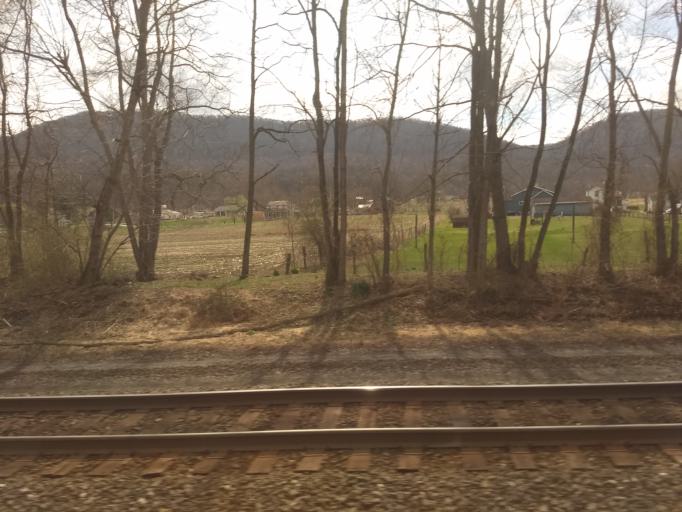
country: US
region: Pennsylvania
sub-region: Huntingdon County
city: Mount Union
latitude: 40.4476
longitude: -77.7495
